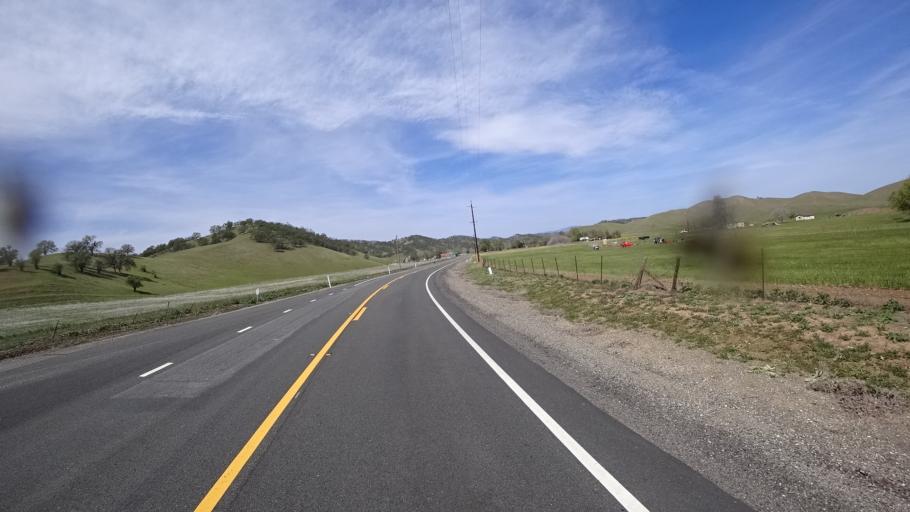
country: US
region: California
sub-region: Glenn County
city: Willows
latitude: 39.5869
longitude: -122.4469
